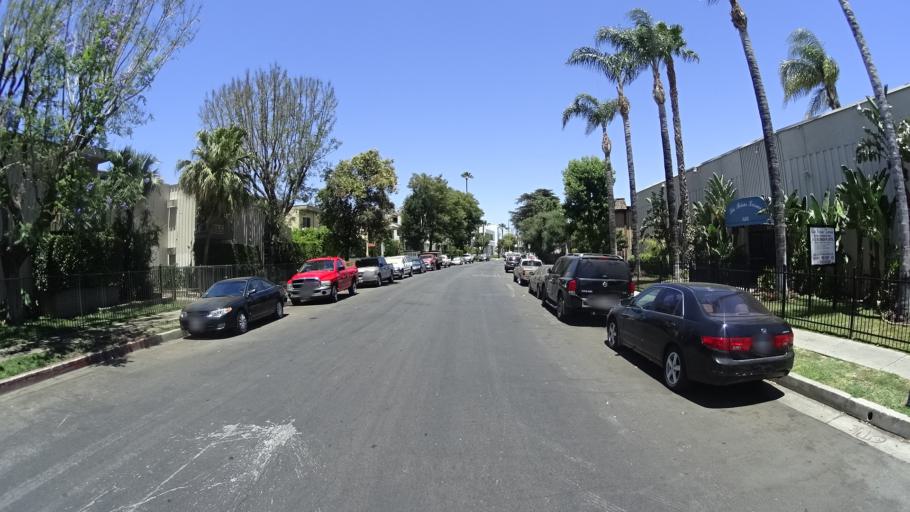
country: US
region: California
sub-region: Los Angeles County
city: Van Nuys
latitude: 34.2193
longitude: -118.4698
